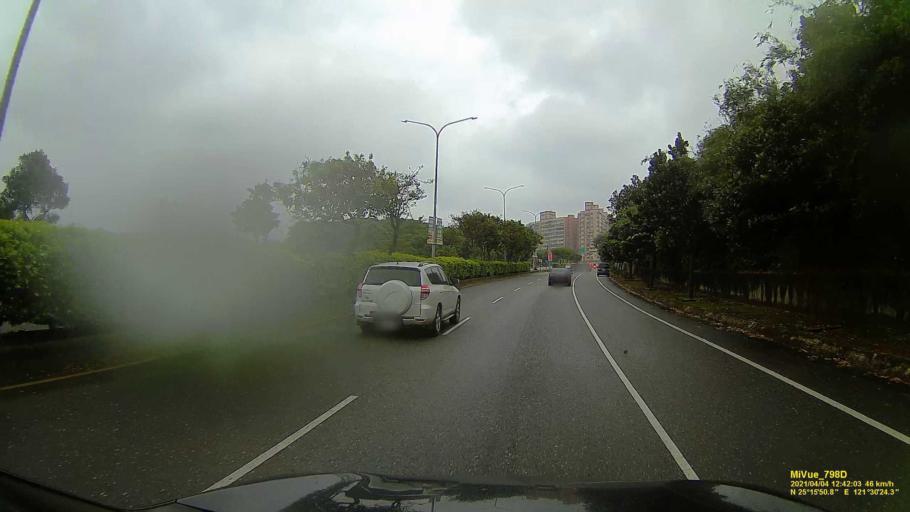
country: TW
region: Taipei
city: Taipei
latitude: 25.2639
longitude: 121.5066
